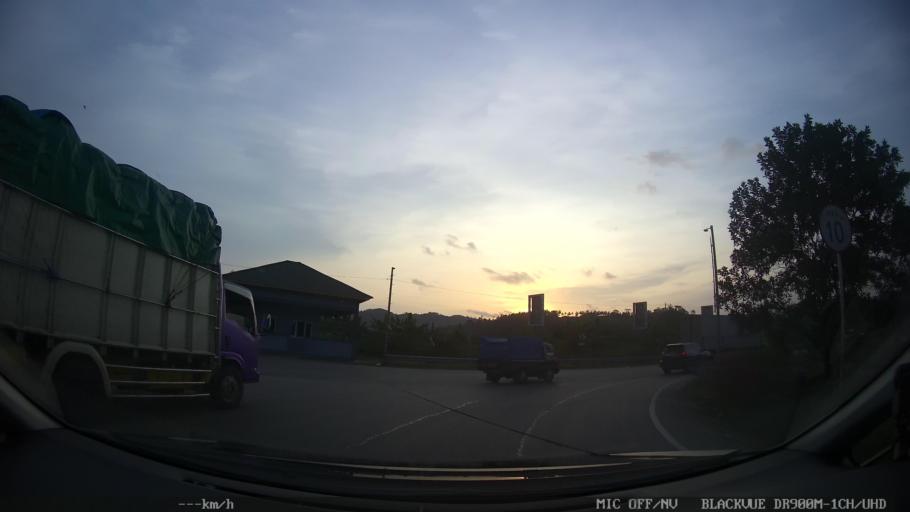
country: ID
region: Lampung
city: Penengahan
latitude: -5.8728
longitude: 105.7503
